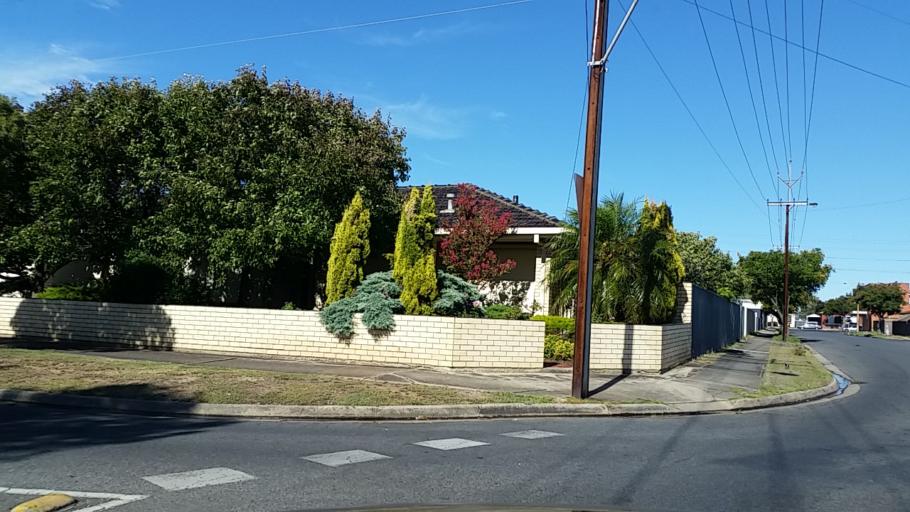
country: AU
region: South Australia
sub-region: Charles Sturt
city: Royal Park
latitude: -34.8693
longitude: 138.5103
